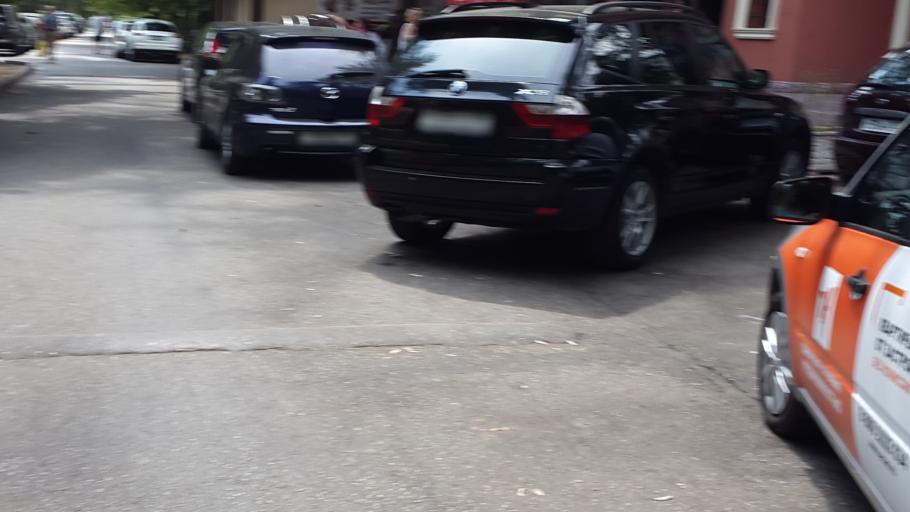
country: RU
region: Krasnodarskiy
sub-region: Sochi City
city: Sochi
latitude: 43.5998
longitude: 39.7241
